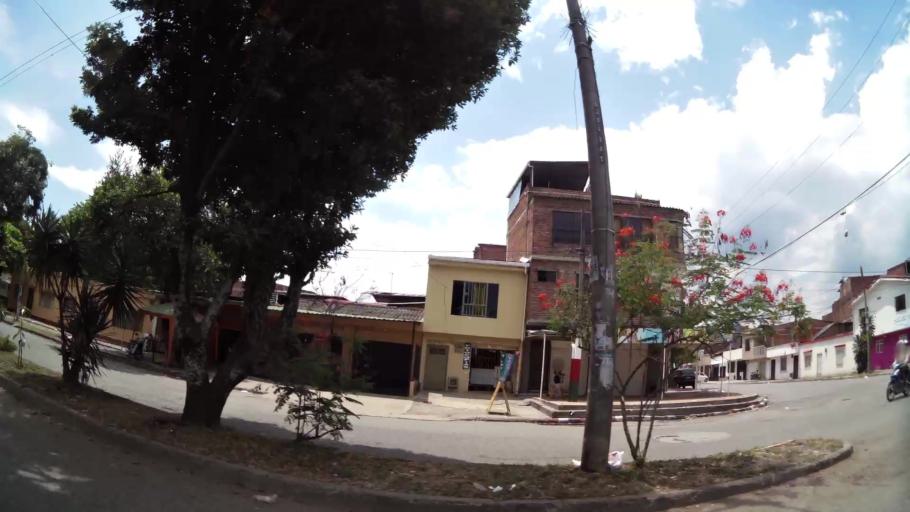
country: CO
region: Valle del Cauca
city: Cali
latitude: 3.4497
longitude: -76.5071
